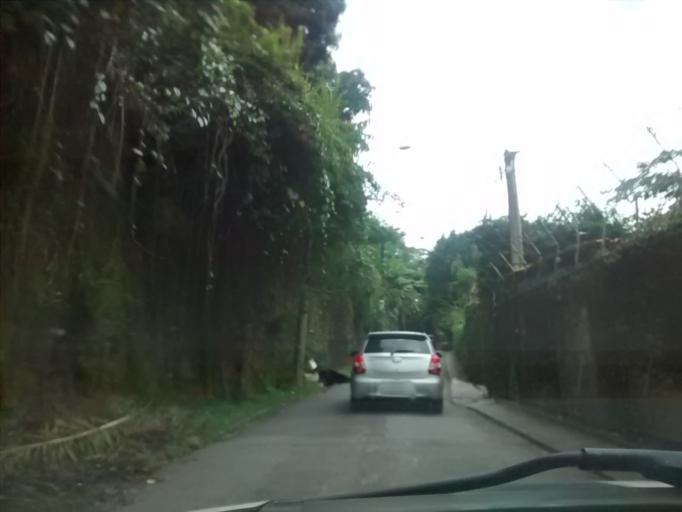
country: BR
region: Rio de Janeiro
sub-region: Rio De Janeiro
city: Rio de Janeiro
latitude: -22.9598
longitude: -43.2707
